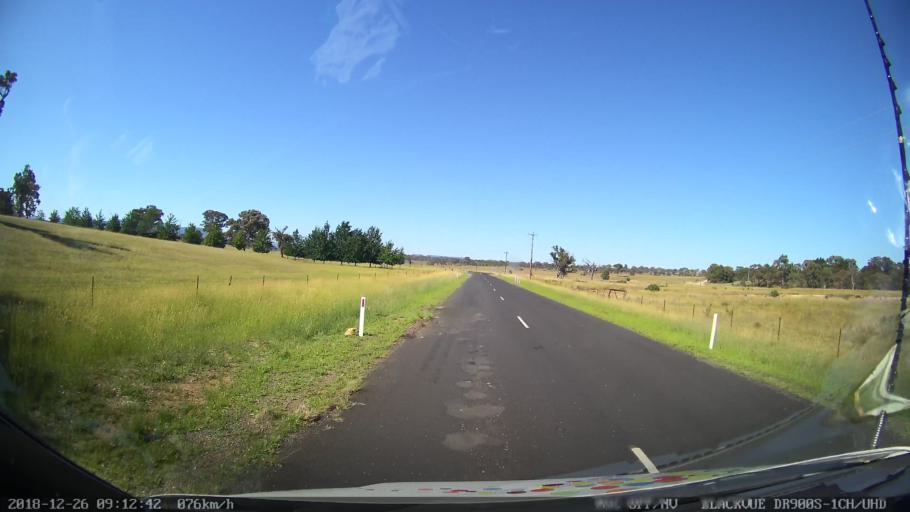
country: AU
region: New South Wales
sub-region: Mid-Western Regional
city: Kandos
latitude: -32.7603
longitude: 149.9804
